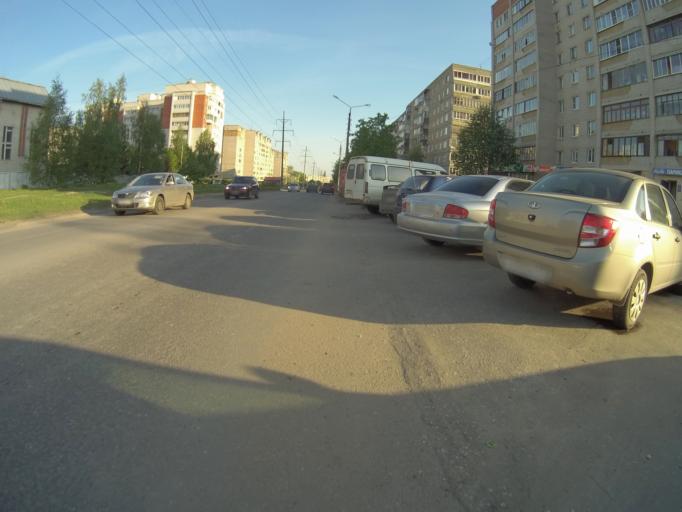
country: RU
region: Vladimir
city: Kommunar
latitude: 56.1648
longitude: 40.4562
